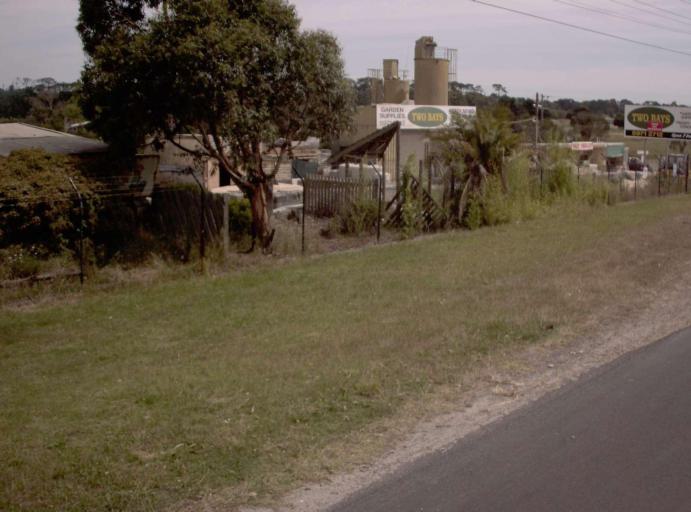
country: AU
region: Victoria
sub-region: Mornington Peninsula
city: Moorooduc
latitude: -38.2028
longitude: 145.1233
